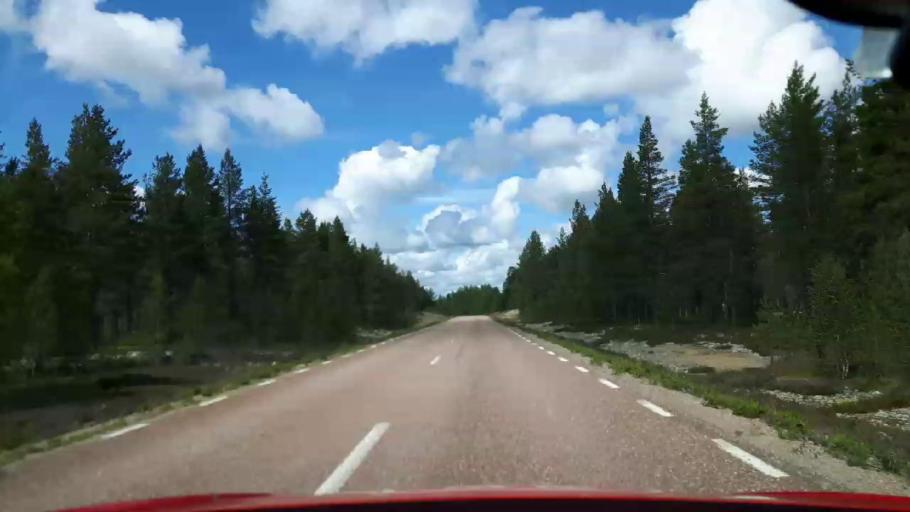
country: SE
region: Dalarna
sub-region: Alvdalens Kommun
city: AElvdalen
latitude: 61.8036
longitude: 13.6577
